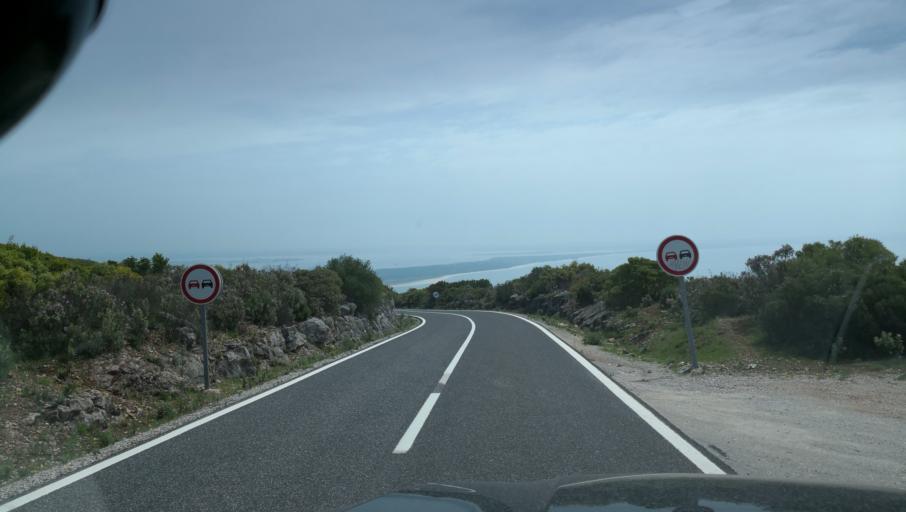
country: PT
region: Setubal
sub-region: Setubal
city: Setubal
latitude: 38.4902
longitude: -8.9561
